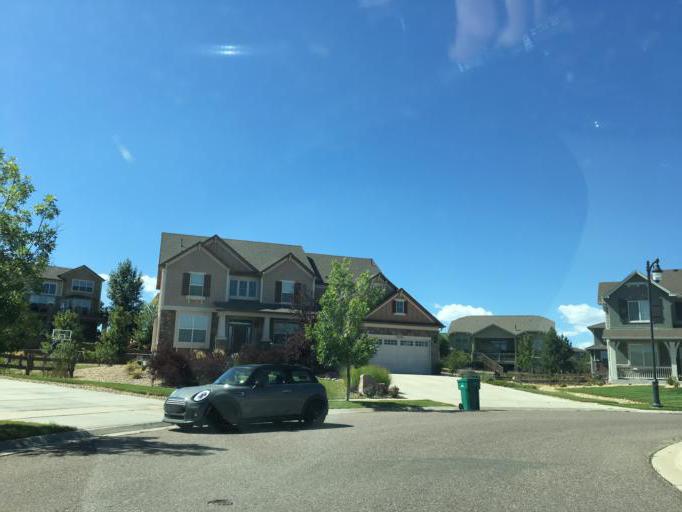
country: US
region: Colorado
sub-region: Douglas County
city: Parker
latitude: 39.5959
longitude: -104.6697
